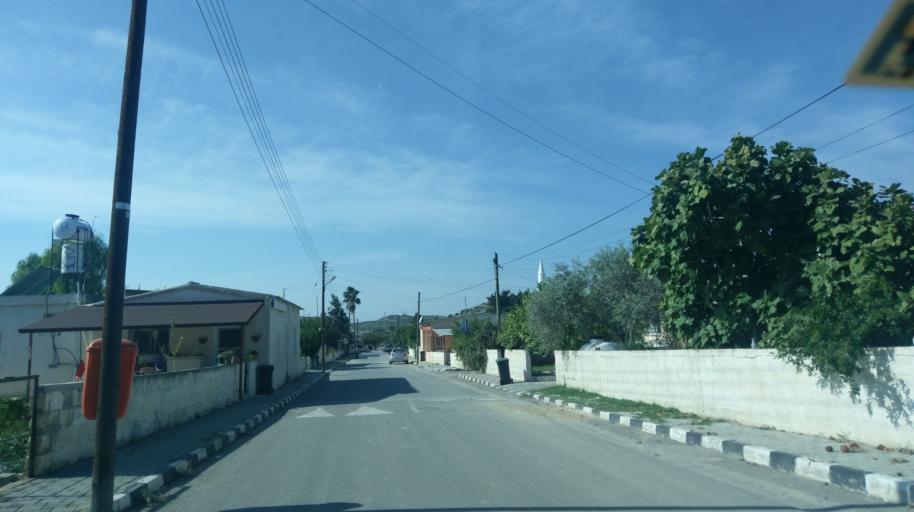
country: CY
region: Ammochostos
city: Trikomo
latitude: 35.3430
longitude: 33.9983
